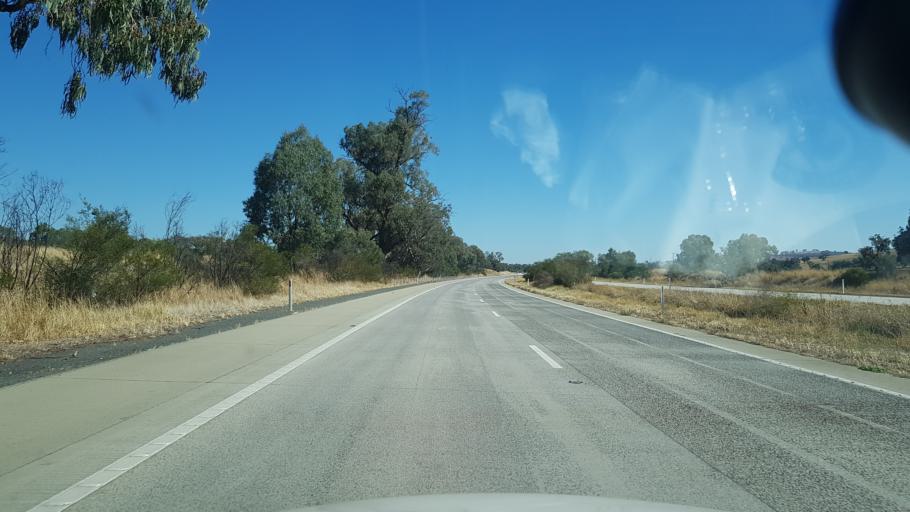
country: AU
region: New South Wales
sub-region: Greater Hume Shire
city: Holbrook
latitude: -35.9041
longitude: 147.1631
